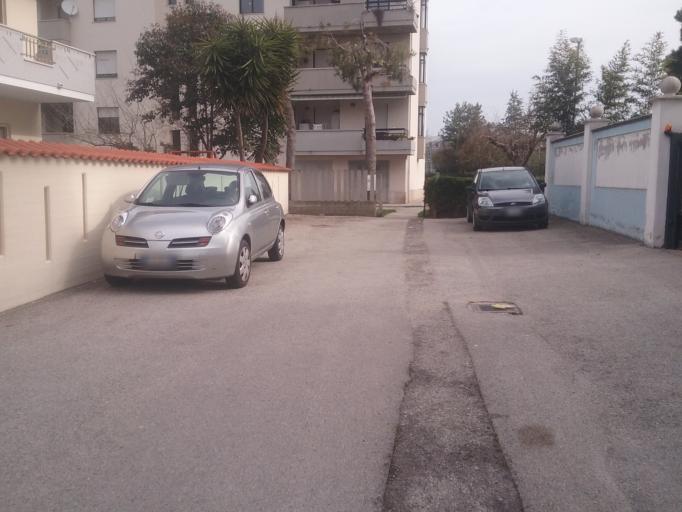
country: IT
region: Abruzzo
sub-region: Provincia di Pescara
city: Montesilvano Marina
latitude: 42.5061
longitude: 14.1419
